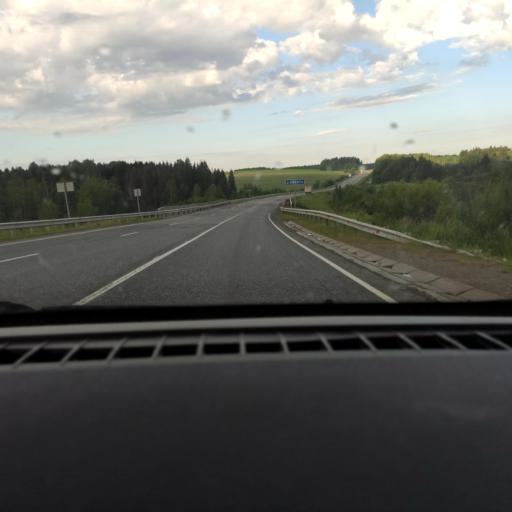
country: RU
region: Udmurtiya
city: Votkinsk
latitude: 57.2336
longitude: 54.1942
